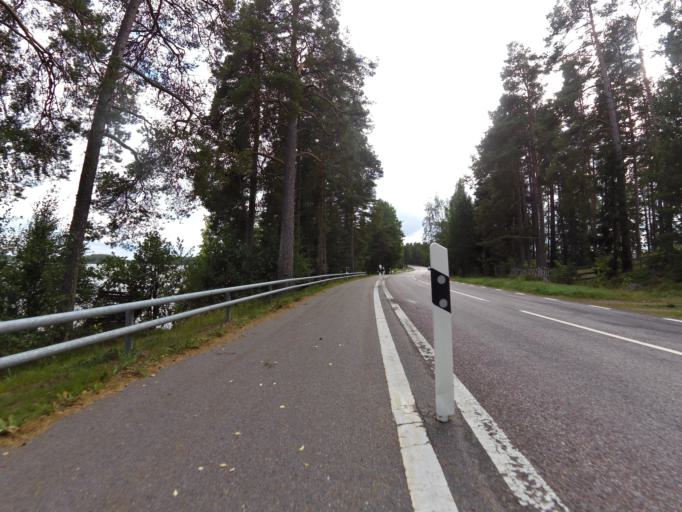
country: SE
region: Gaevleborg
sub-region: Sandvikens Kommun
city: Sandviken
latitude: 60.6990
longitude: 16.8174
